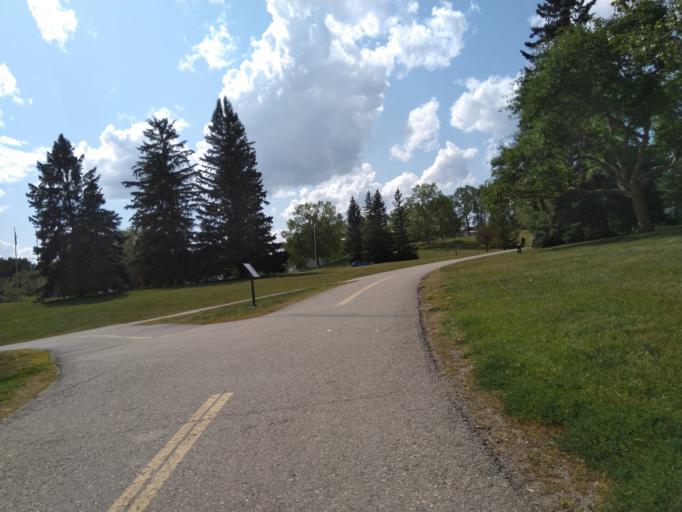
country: CA
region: Alberta
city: Calgary
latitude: 51.0772
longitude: -114.0831
